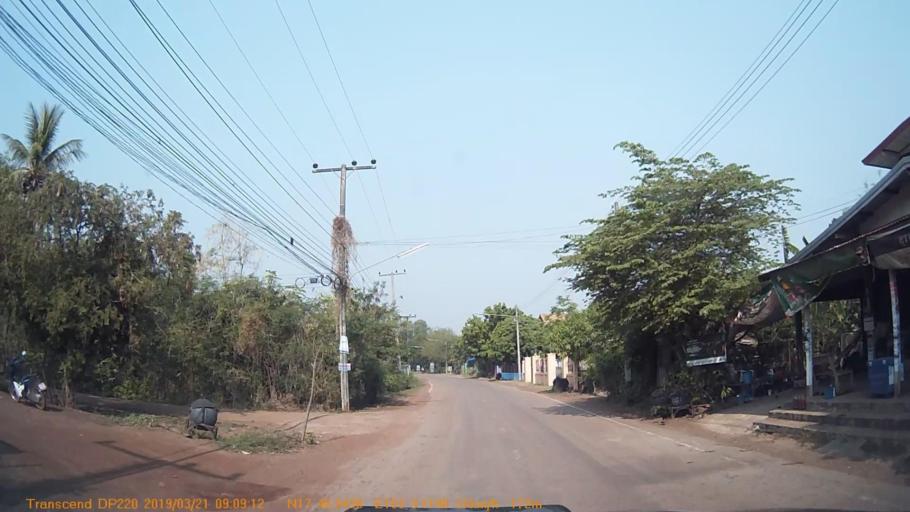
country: TH
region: Changwat Udon Thani
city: Phibun Rak
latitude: 17.6824
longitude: 103.0517
